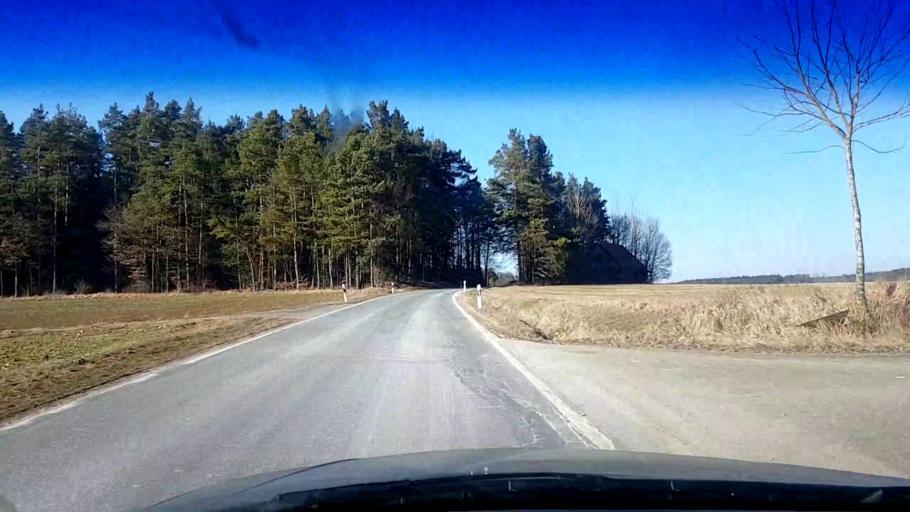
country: DE
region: Bavaria
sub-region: Upper Franconia
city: Aufsess
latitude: 49.9193
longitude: 11.2196
